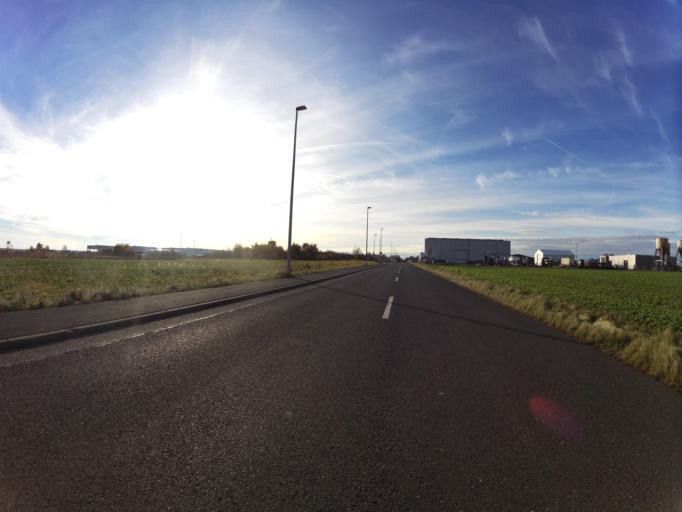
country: DE
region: Bavaria
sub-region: Regierungsbezirk Unterfranken
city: Giebelstadt
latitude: 49.6550
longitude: 9.9614
